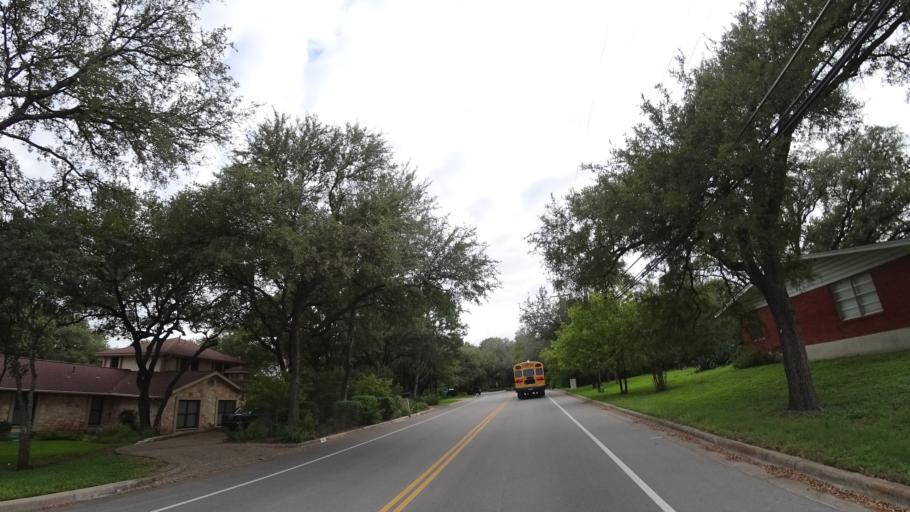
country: US
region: Texas
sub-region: Travis County
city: Rollingwood
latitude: 30.2753
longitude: -97.7923
